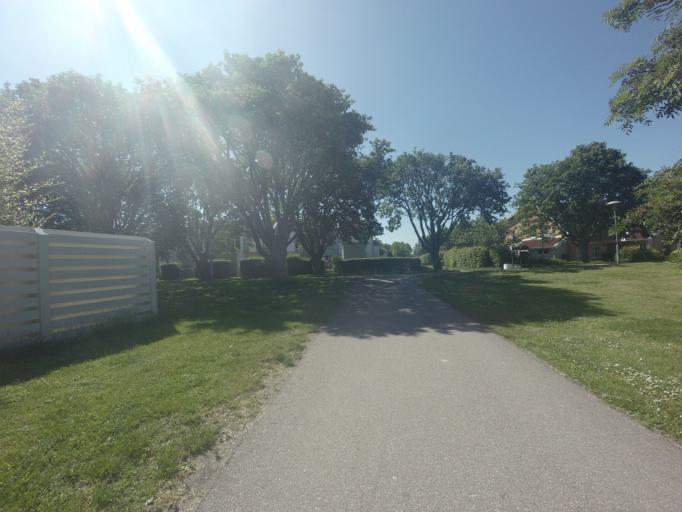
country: SE
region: Skane
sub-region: Malmo
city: Bunkeflostrand
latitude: 55.5232
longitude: 12.9356
